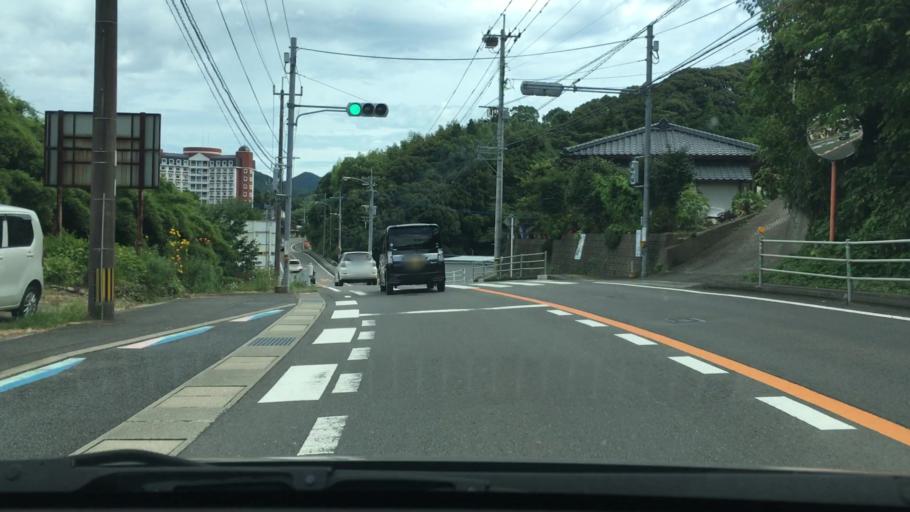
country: JP
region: Nagasaki
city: Togitsu
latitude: 32.8816
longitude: 129.7891
